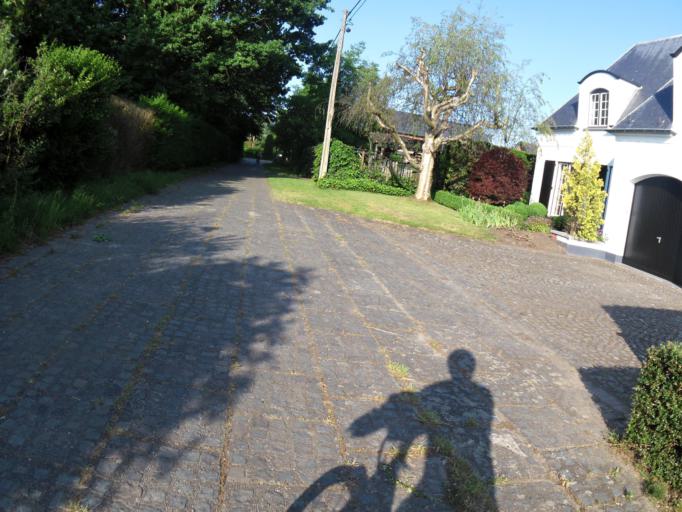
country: BE
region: Flanders
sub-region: Provincie Antwerpen
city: Geel
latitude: 51.1561
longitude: 4.9814
